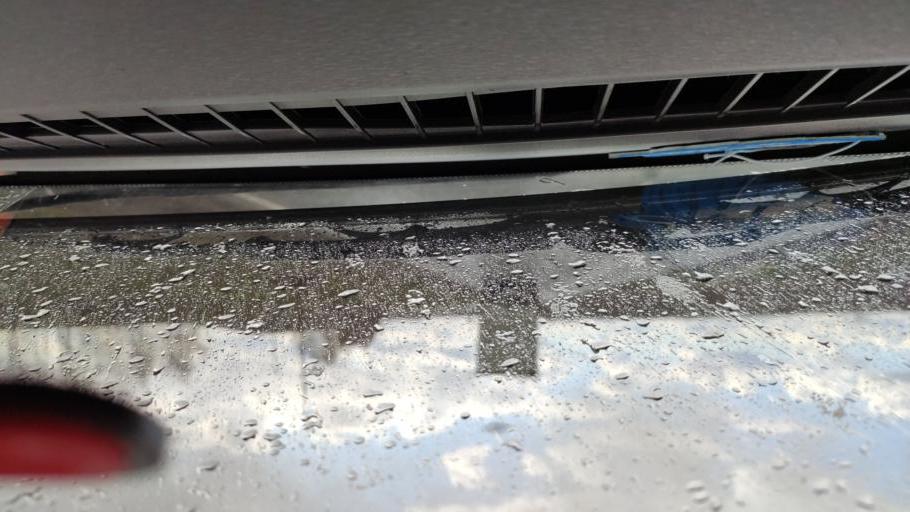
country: RU
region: Saratov
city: Balakovo
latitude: 52.1106
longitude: 47.7482
